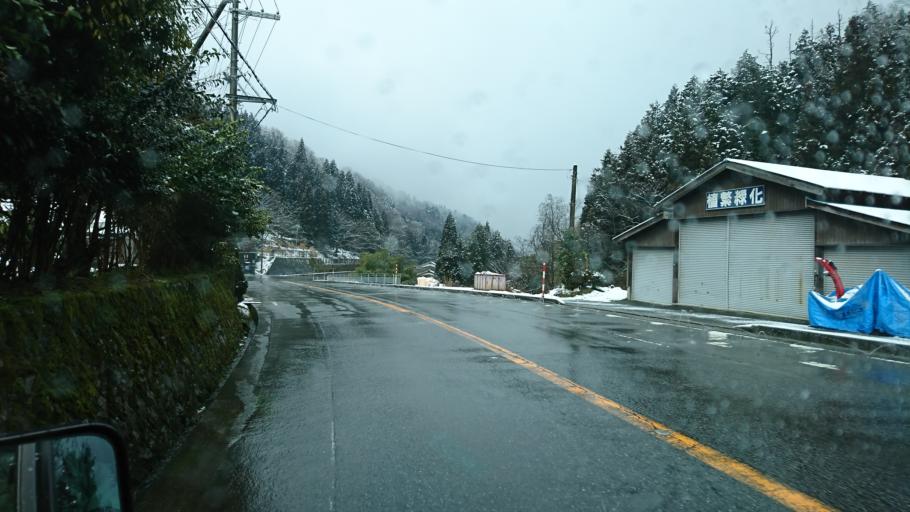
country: JP
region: Tottori
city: Tottori
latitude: 35.5247
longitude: 134.5205
